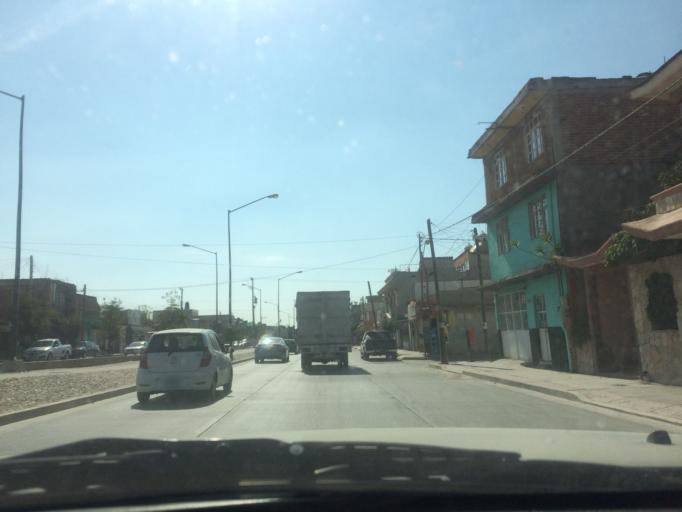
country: MX
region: Guanajuato
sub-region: Leon
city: Medina
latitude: 21.1432
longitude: -101.6458
